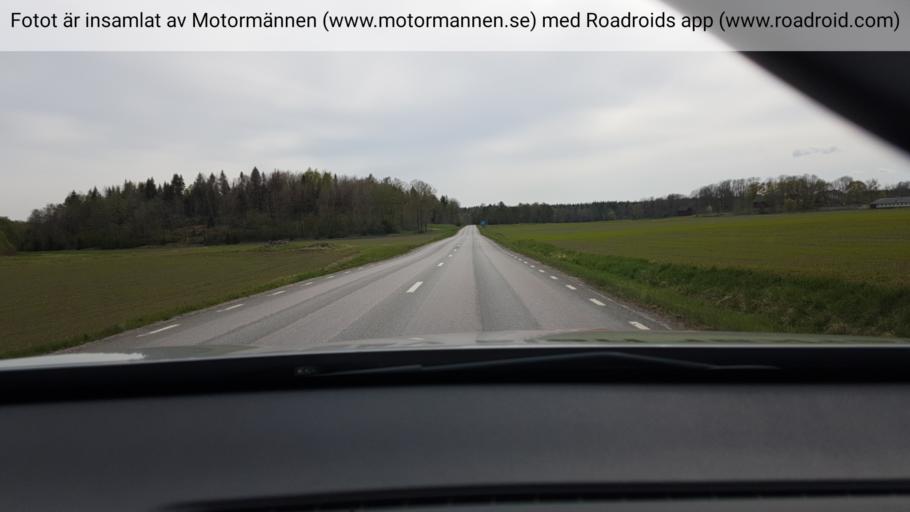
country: SE
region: Stockholm
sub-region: Norrtalje Kommun
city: Nykvarn
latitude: 59.9245
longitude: 18.1078
